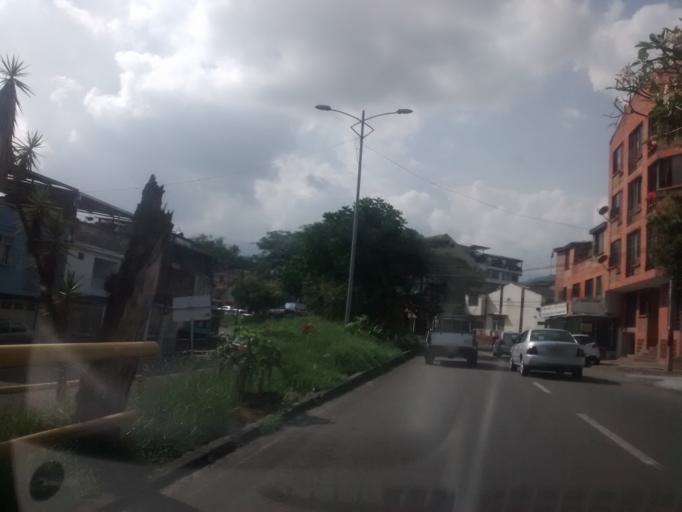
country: CO
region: Tolima
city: Ibague
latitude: 4.4425
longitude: -75.2236
